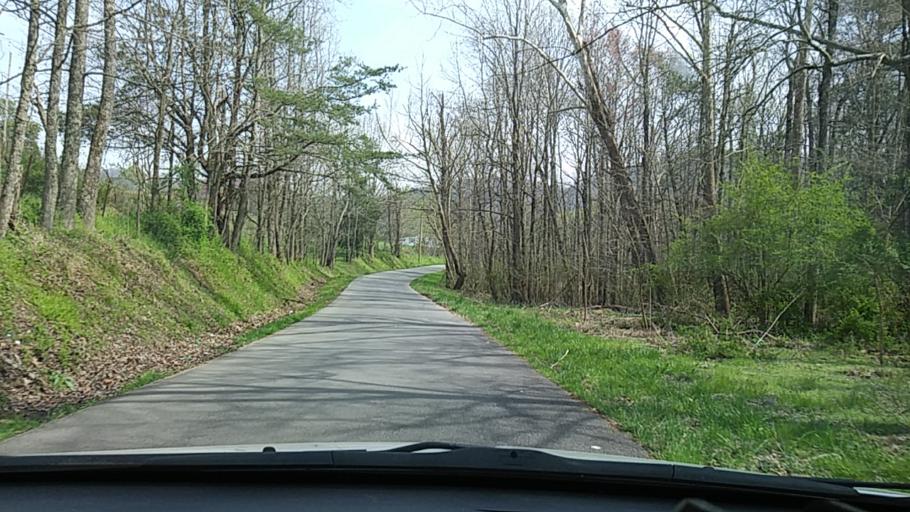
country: US
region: Tennessee
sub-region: Greene County
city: Tusculum
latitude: 36.0963
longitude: -82.7081
